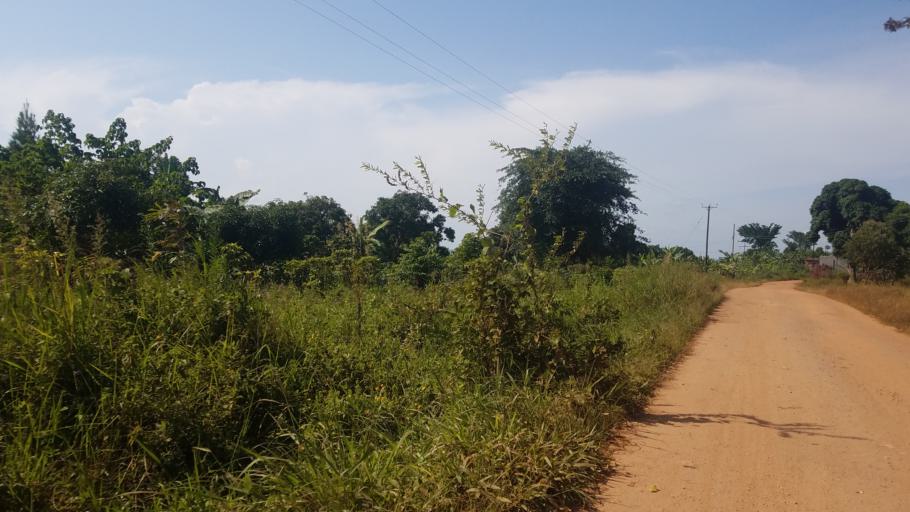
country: UG
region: Central Region
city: Masaka
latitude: -0.3040
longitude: 31.6831
